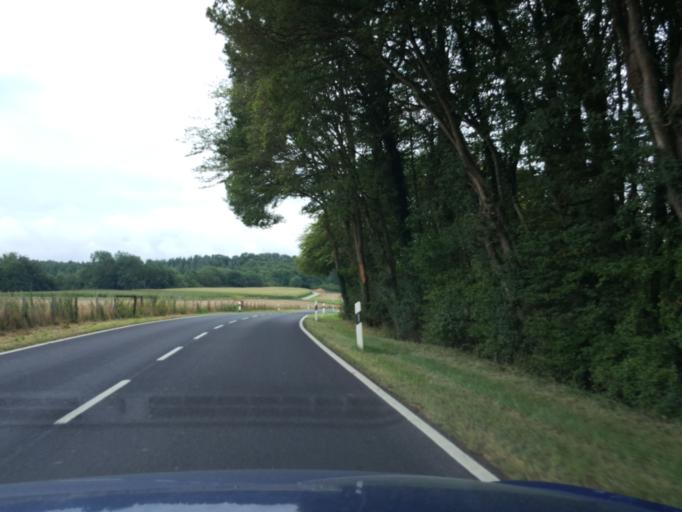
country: LU
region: Luxembourg
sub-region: Canton de Capellen
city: Kehlen
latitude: 49.6595
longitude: 6.0349
